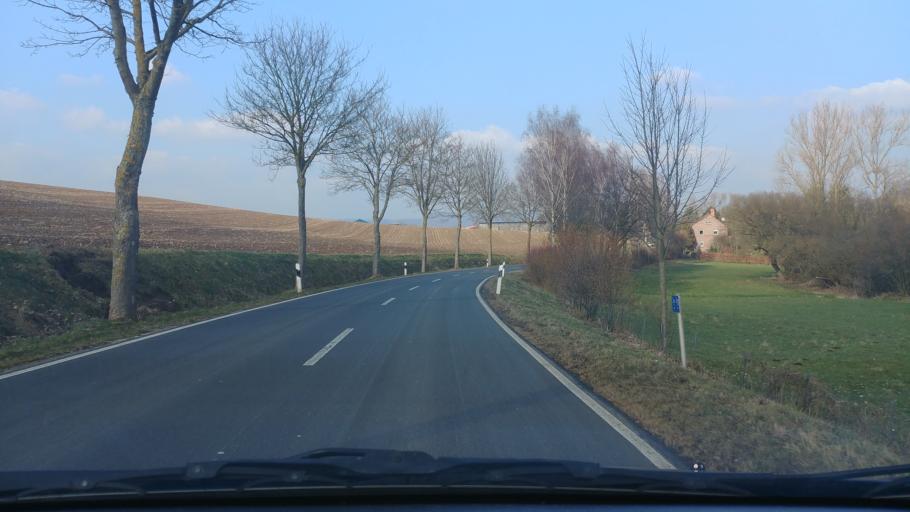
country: DE
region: Lower Saxony
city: Dassel
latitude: 51.7716
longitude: 9.6859
